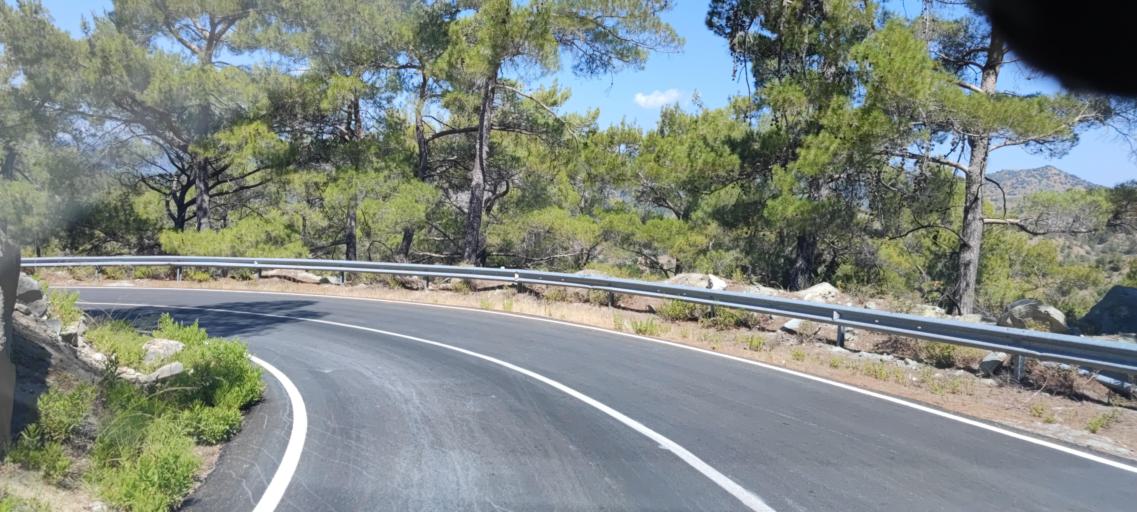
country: CY
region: Lefkosia
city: Kakopetria
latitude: 34.9219
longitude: 32.8100
